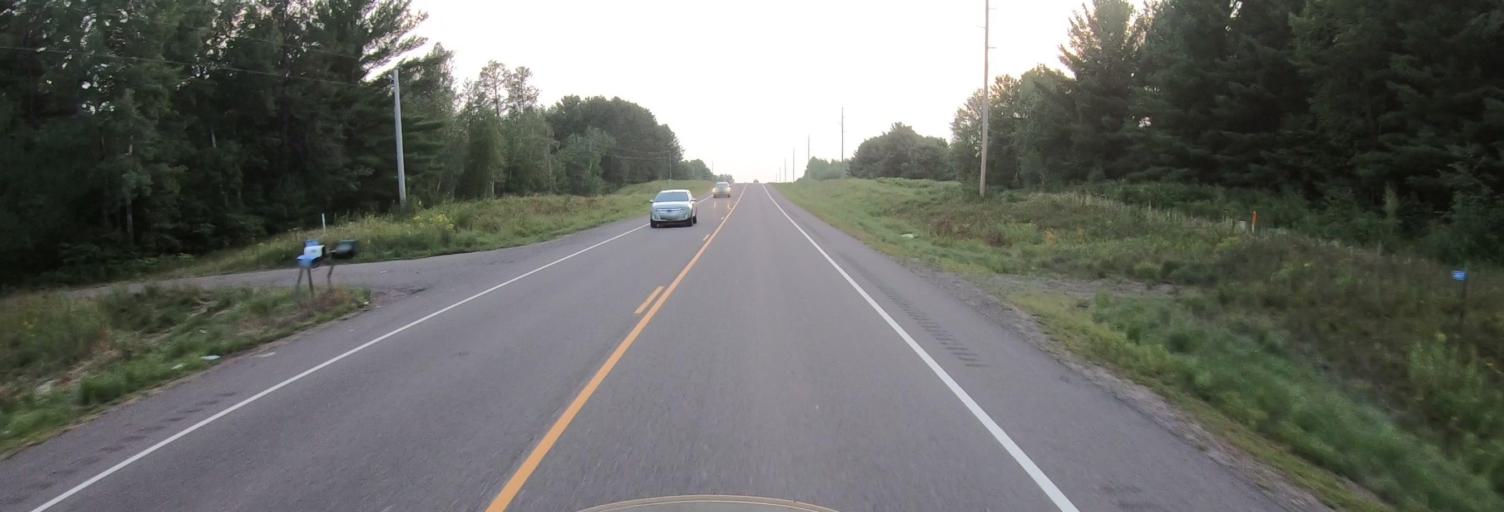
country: US
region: Wisconsin
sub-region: Burnett County
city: Grantsburg
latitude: 45.7736
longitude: -92.8081
